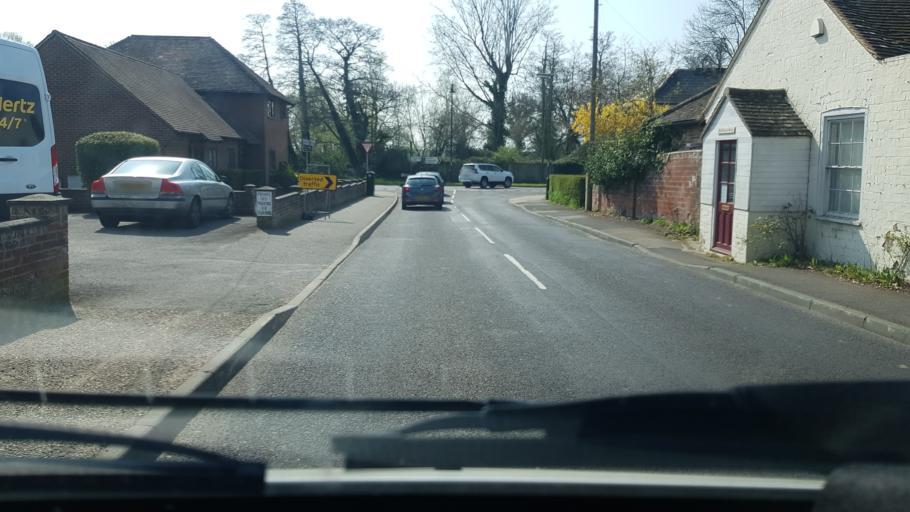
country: GB
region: England
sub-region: West Sussex
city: Chichester
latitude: 50.8363
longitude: -0.8154
